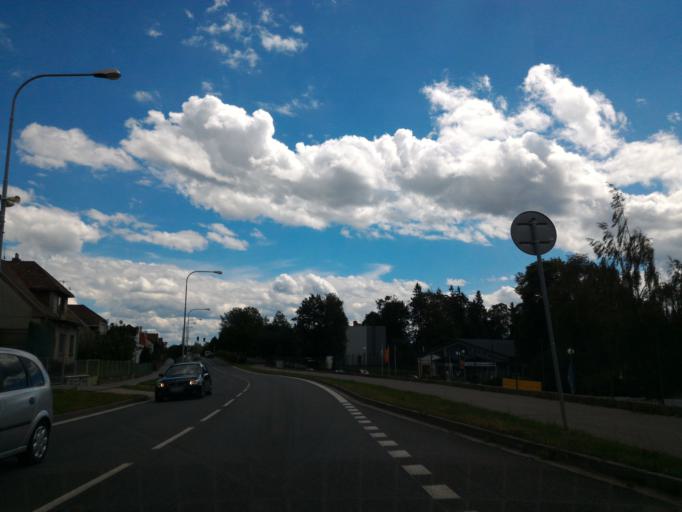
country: CZ
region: Vysocina
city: Zd'ar nad Sazavou Druhy
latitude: 49.5769
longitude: 15.9383
